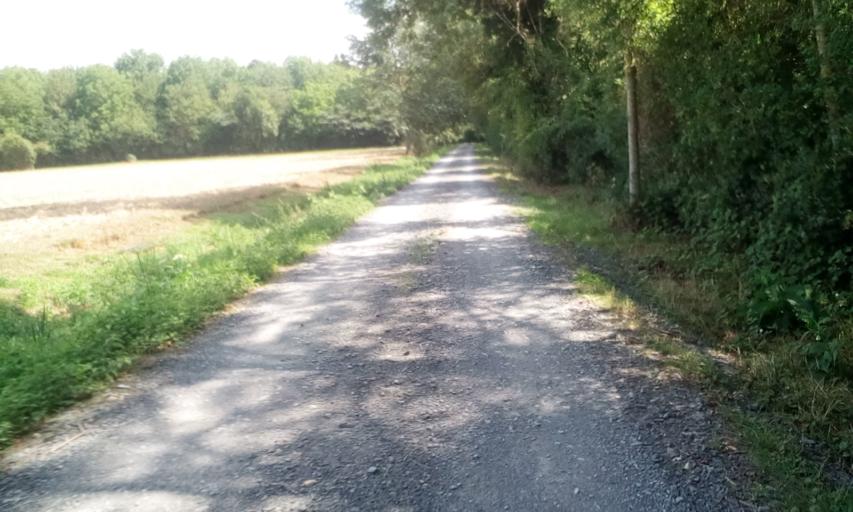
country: FR
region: Lower Normandy
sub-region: Departement du Calvados
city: Argences
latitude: 49.1416
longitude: -0.1683
